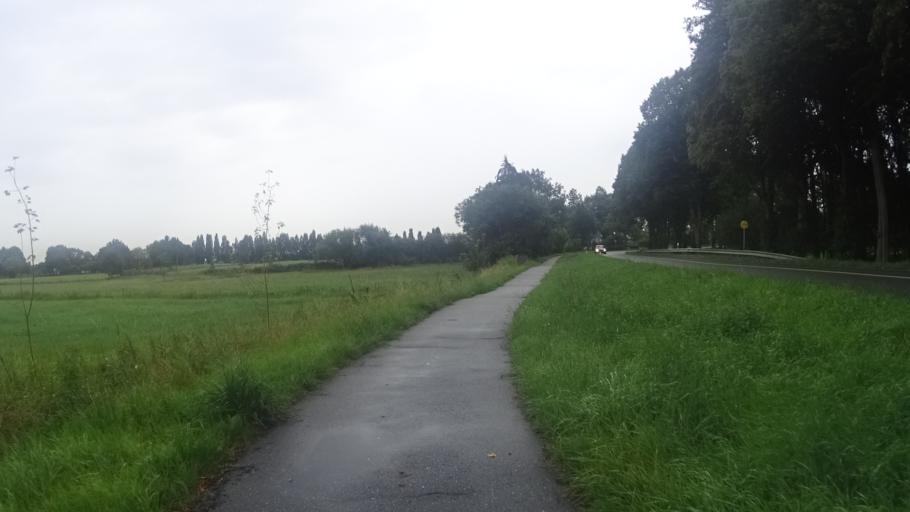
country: DE
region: Schleswig-Holstein
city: Seeth-Ekholt
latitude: 53.7564
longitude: 9.7297
